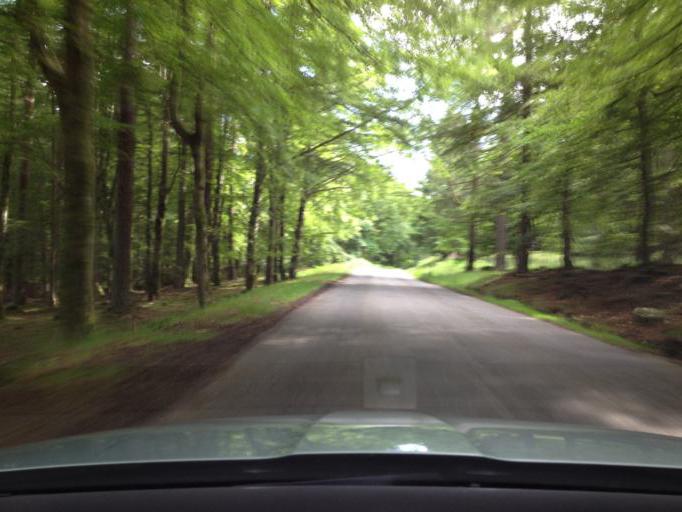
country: GB
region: Scotland
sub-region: Aberdeenshire
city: Banchory
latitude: 56.9761
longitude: -2.5749
